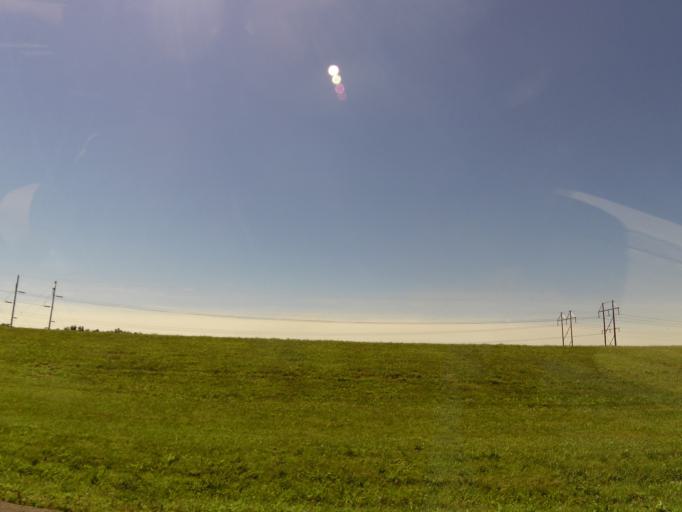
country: US
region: Missouri
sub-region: New Madrid County
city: New Madrid
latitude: 36.5744
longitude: -89.5690
